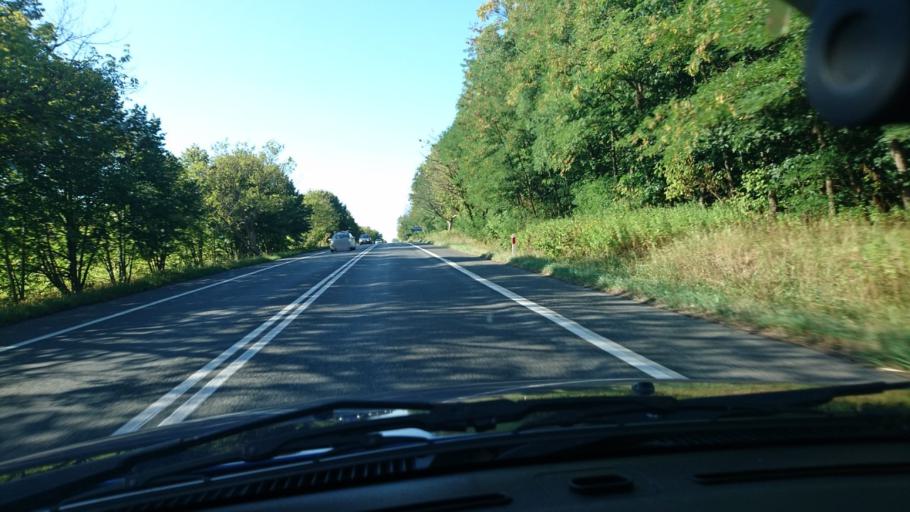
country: PL
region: Silesian Voivodeship
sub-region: Powiat gliwicki
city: Pyskowice
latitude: 50.3557
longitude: 18.6442
